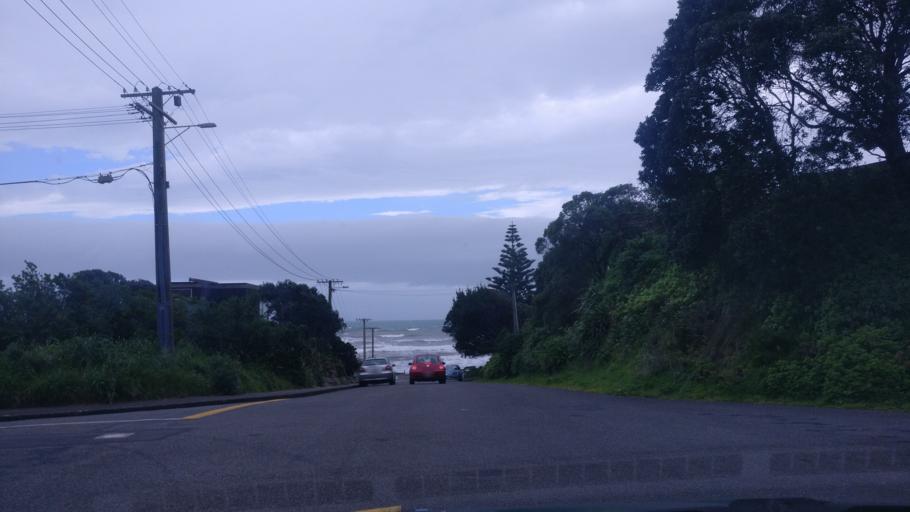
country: NZ
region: Wellington
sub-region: Kapiti Coast District
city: Paraparaumu
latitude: -40.9760
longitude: 174.9595
